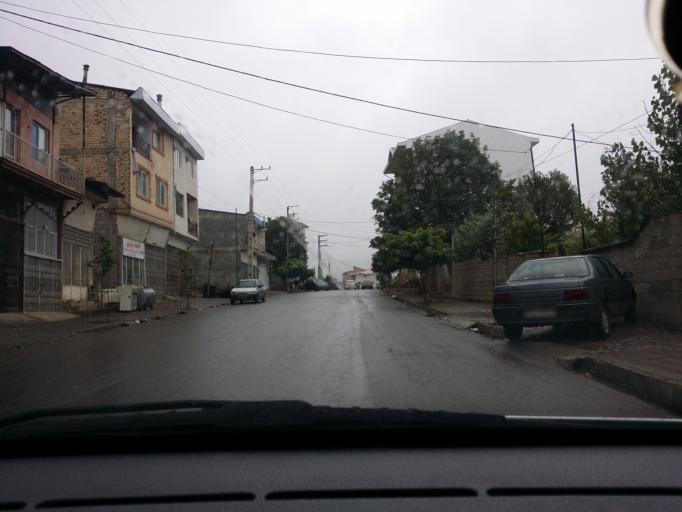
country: IR
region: Mazandaran
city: Chalus
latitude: 36.5255
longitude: 51.2322
